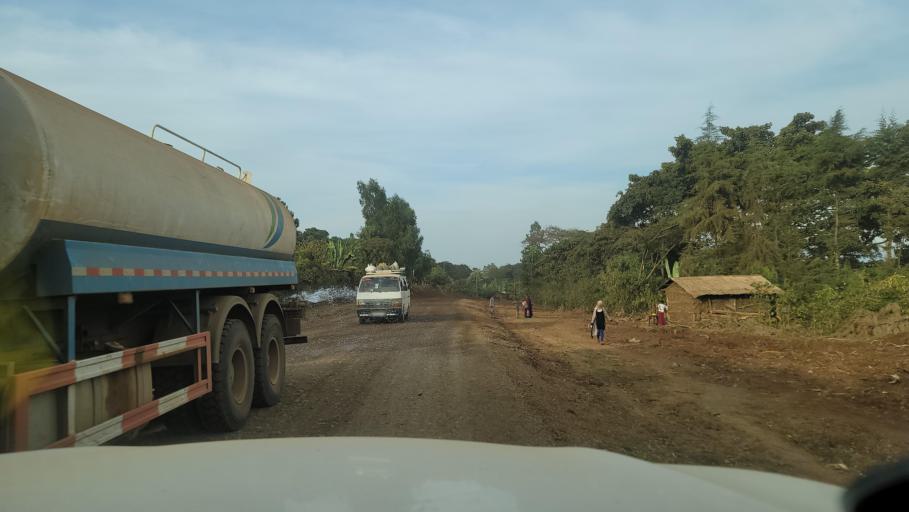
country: ET
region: Oromiya
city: Agaro
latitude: 7.8230
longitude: 36.5385
